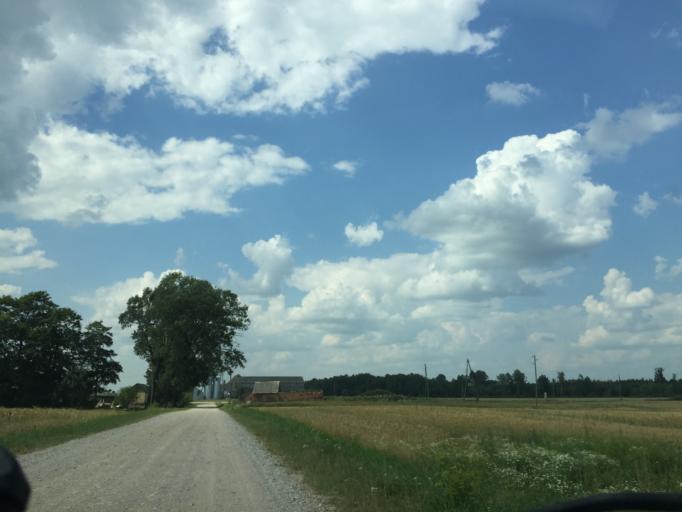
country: LT
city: Zagare
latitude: 56.3343
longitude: 23.0819
